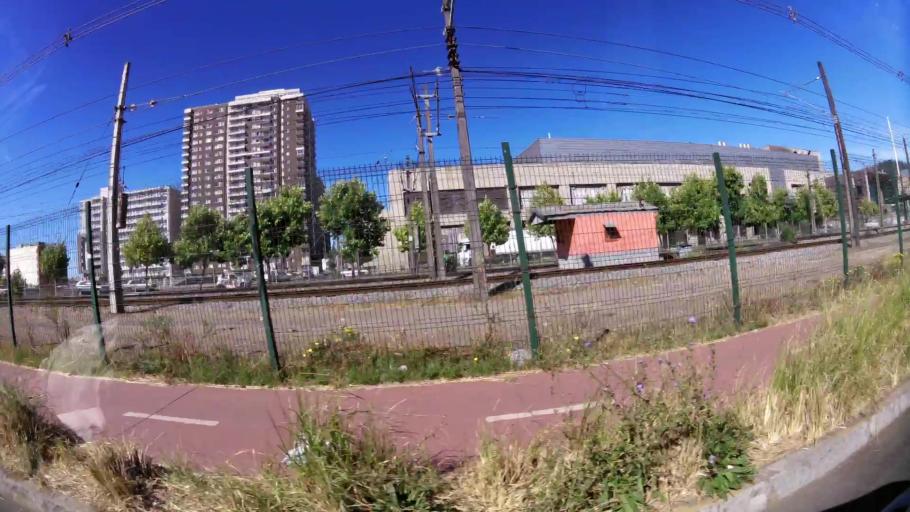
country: CL
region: Biobio
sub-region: Provincia de Concepcion
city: Concepcion
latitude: -36.8289
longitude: -73.0621
